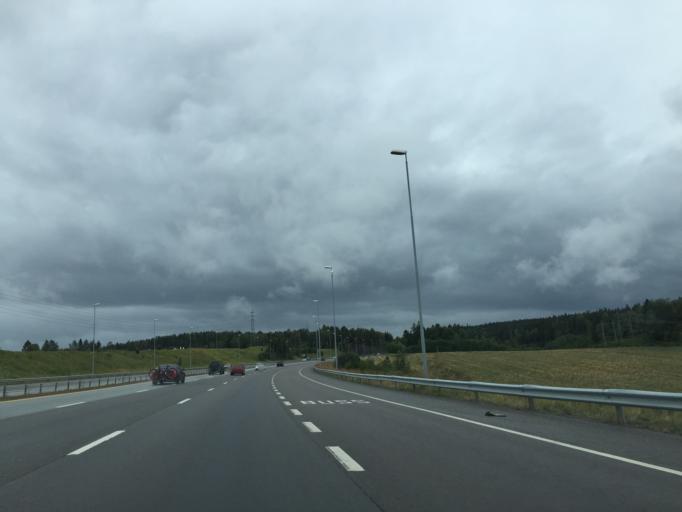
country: NO
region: Akershus
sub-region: Lorenskog
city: Kjenn
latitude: 59.9669
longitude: 10.9866
